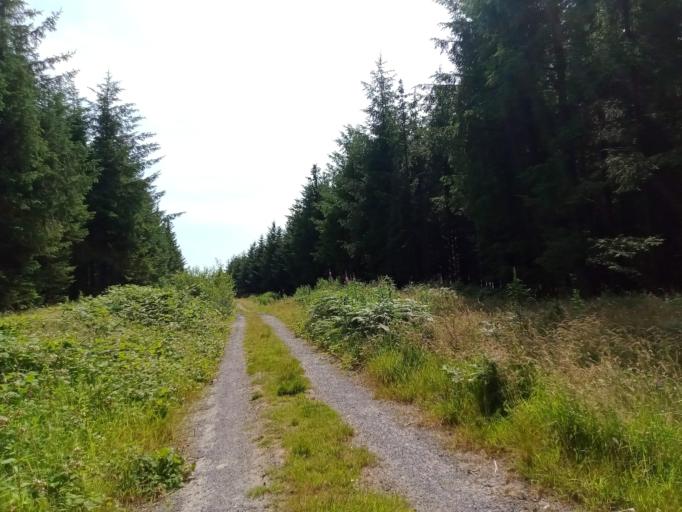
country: IE
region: Leinster
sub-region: Kilkenny
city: Ballyragget
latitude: 52.8038
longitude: -7.4541
